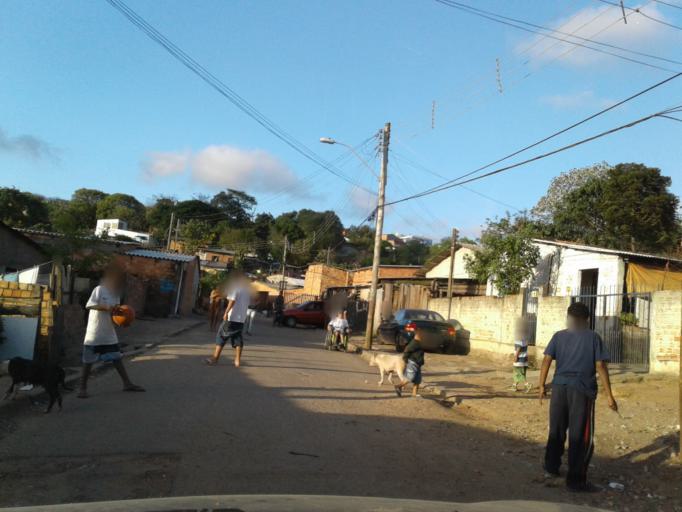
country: BR
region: Rio Grande do Sul
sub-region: Porto Alegre
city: Porto Alegre
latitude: -30.0485
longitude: -51.1532
